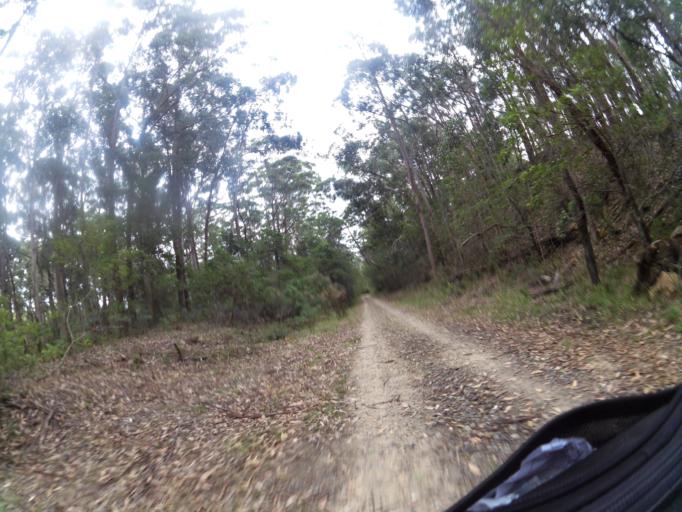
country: AU
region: Victoria
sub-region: East Gippsland
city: Lakes Entrance
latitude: -37.7310
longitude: 148.4263
